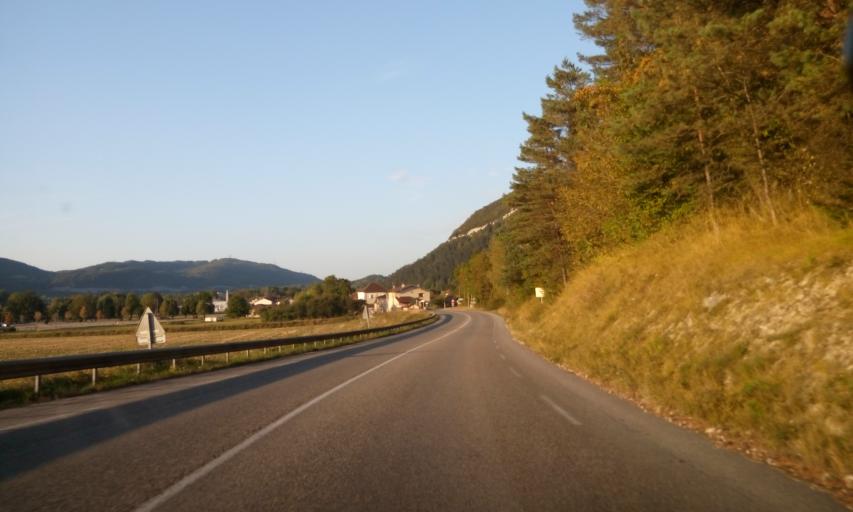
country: FR
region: Rhone-Alpes
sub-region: Departement de l'Ain
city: Saint-Martin-du-Frene
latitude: 46.1581
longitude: 5.5684
